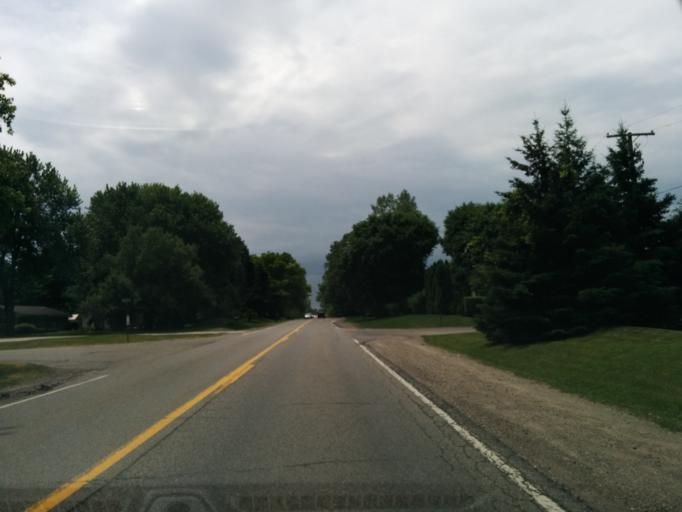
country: US
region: Michigan
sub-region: Oakland County
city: Wolverine Lake
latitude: 42.5494
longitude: -83.4585
